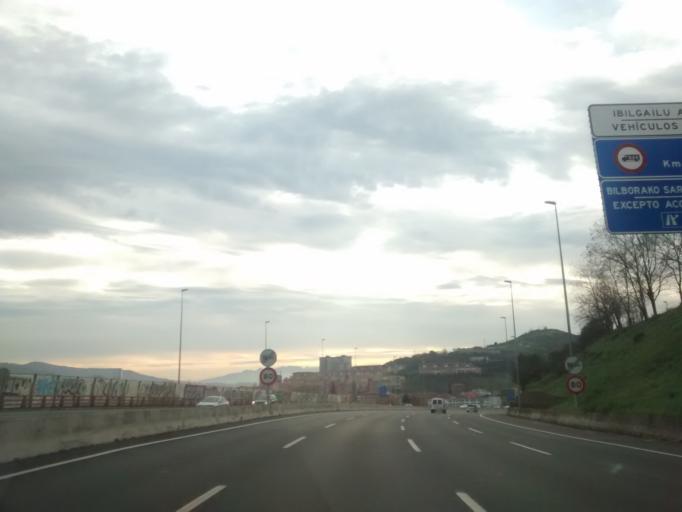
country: ES
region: Basque Country
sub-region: Bizkaia
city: Barakaldo
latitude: 43.2783
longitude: -2.9816
